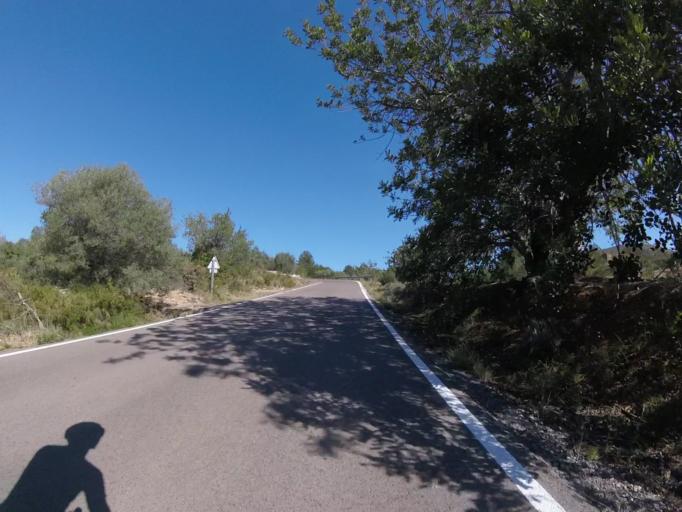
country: ES
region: Valencia
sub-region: Provincia de Castello
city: Santa Magdalena de Pulpis
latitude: 40.3730
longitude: 0.2725
